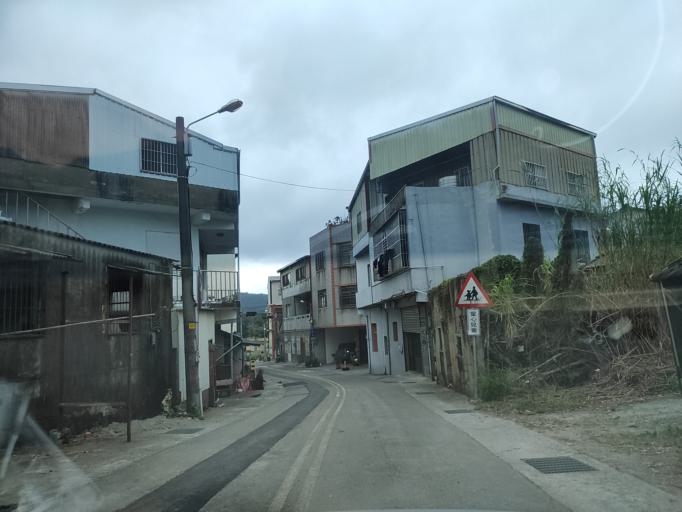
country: TW
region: Taiwan
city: Fengyuan
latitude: 24.3830
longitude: 120.7584
